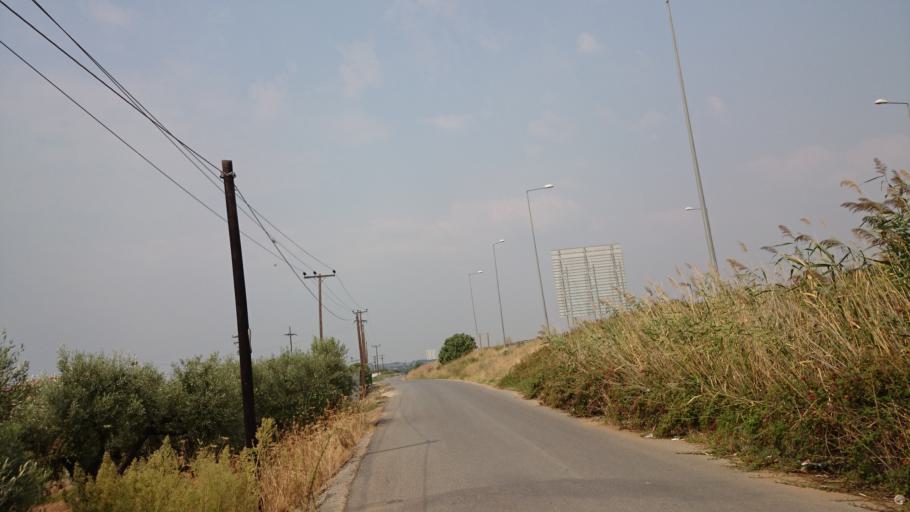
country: GR
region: Central Macedonia
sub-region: Nomos Chalkidikis
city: Nea Moudhania
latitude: 40.2609
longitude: 23.2717
